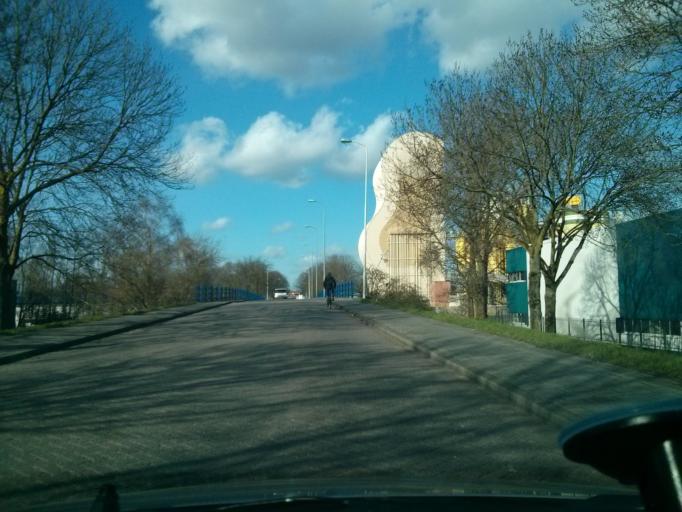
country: NL
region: North Brabant
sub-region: Gemeente Eindhoven
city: Meerhoven
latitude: 51.4339
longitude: 5.4398
